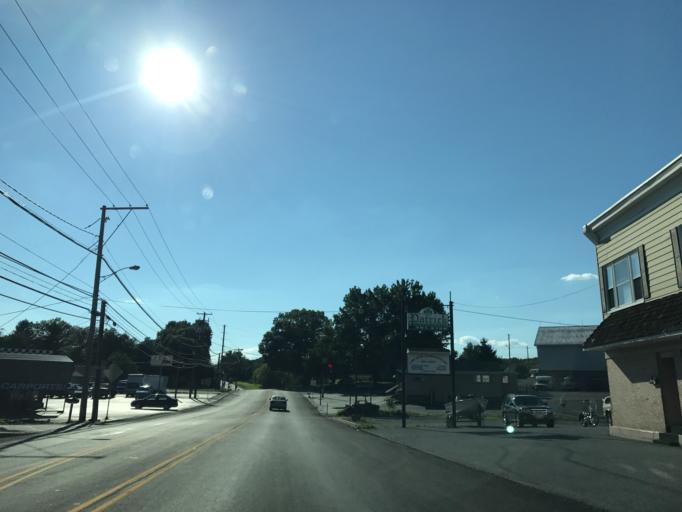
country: US
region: Pennsylvania
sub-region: Lancaster County
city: Elizabethtown
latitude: 40.1577
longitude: -76.6111
